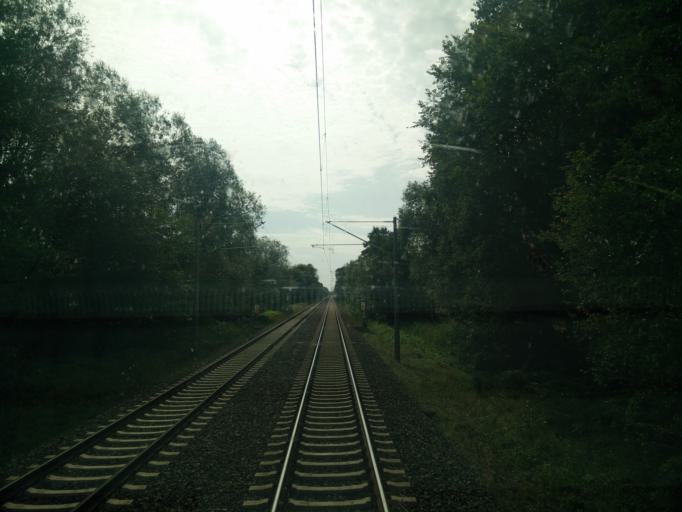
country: DE
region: Brandenburg
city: Luebben
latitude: 51.9074
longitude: 13.9023
